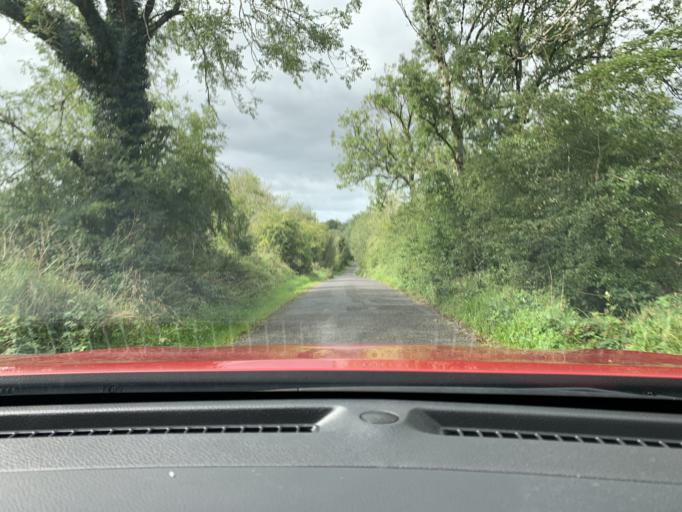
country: IE
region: Connaught
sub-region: Sligo
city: Collooney
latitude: 54.1560
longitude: -8.4263
